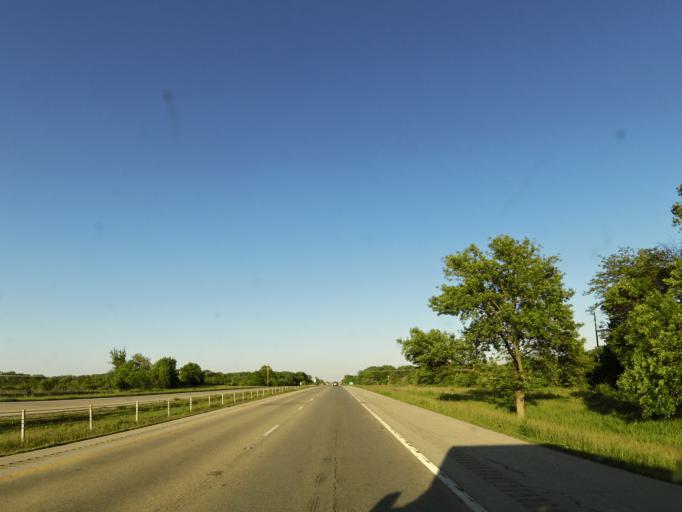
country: US
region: Illinois
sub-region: Champaign County
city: Saint Joseph
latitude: 40.1204
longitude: -88.0619
